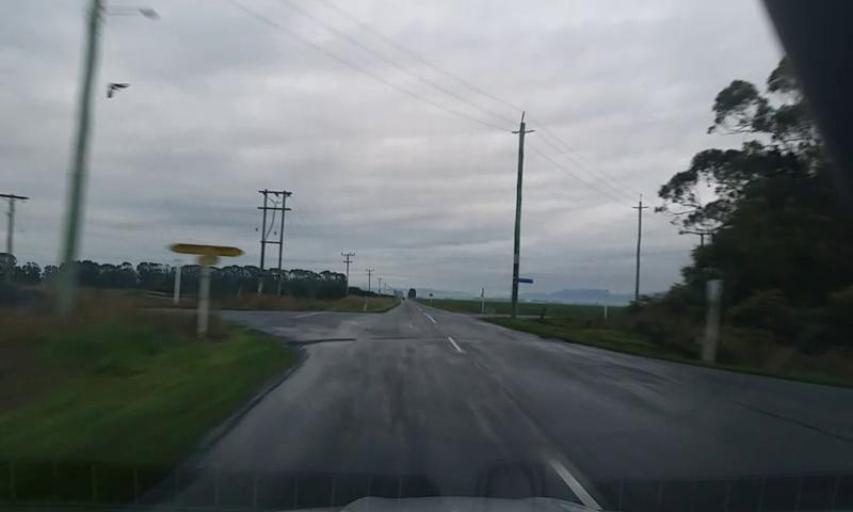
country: NZ
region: Canterbury
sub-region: Ashburton District
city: Rakaia
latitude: -43.7527
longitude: 171.8621
